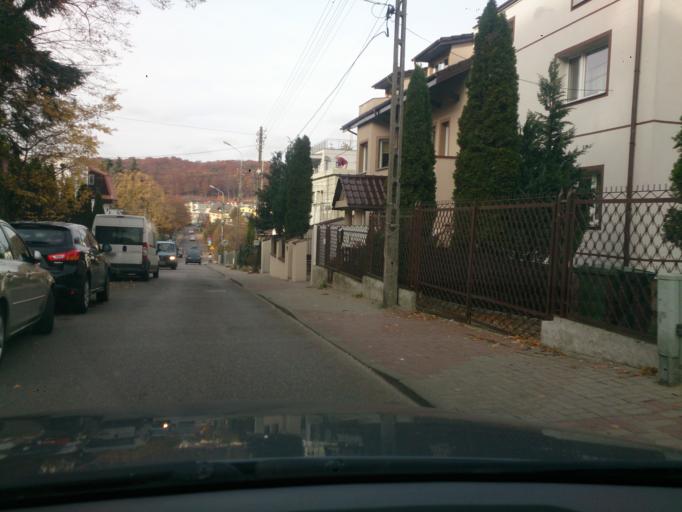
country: PL
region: Pomeranian Voivodeship
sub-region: Gdynia
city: Gdynia
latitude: 54.4834
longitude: 18.5289
